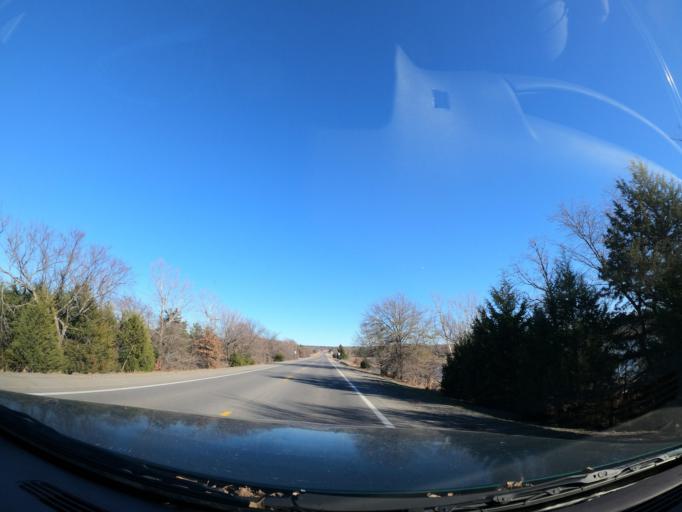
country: US
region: Oklahoma
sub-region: Pittsburg County
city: Longtown
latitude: 35.2392
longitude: -95.4890
